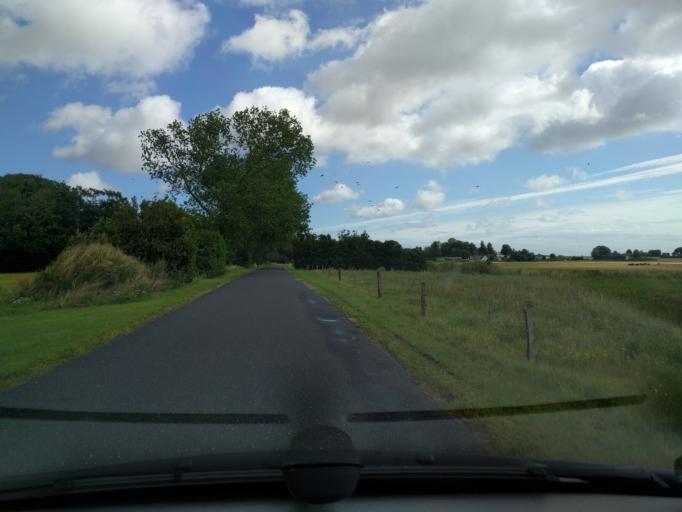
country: DK
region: South Denmark
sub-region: Kerteminde Kommune
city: Langeskov
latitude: 55.3880
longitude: 10.5915
